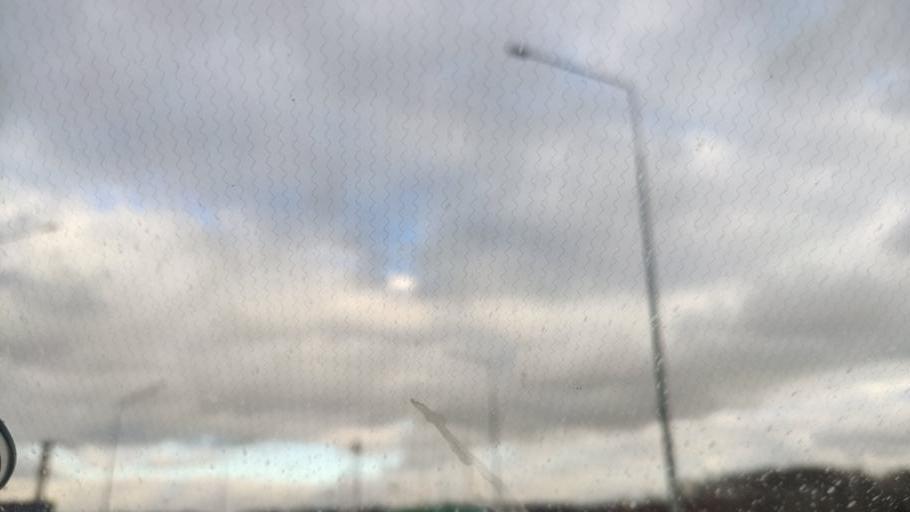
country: RU
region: Moskovskaya
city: Mosrentgen
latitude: 55.6054
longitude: 37.4244
